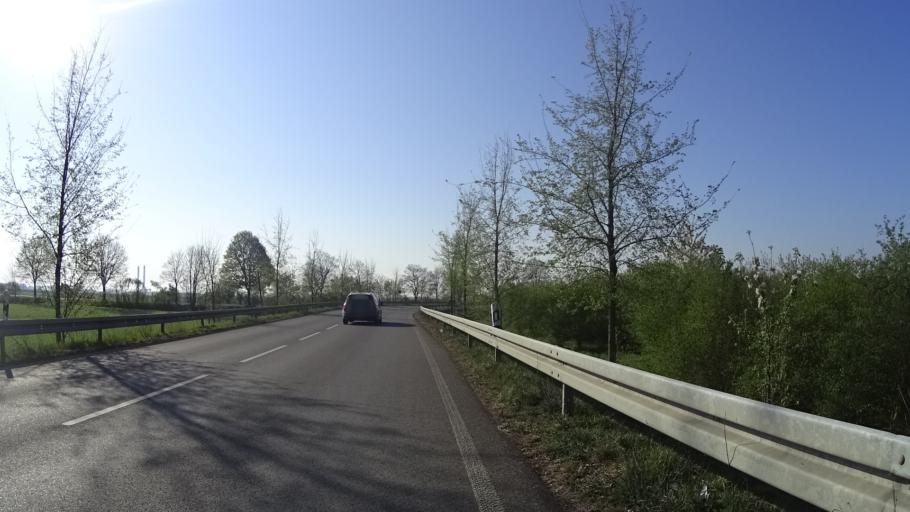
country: DE
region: North Rhine-Westphalia
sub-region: Regierungsbezirk Dusseldorf
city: Wesel
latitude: 51.6369
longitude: 6.5886
